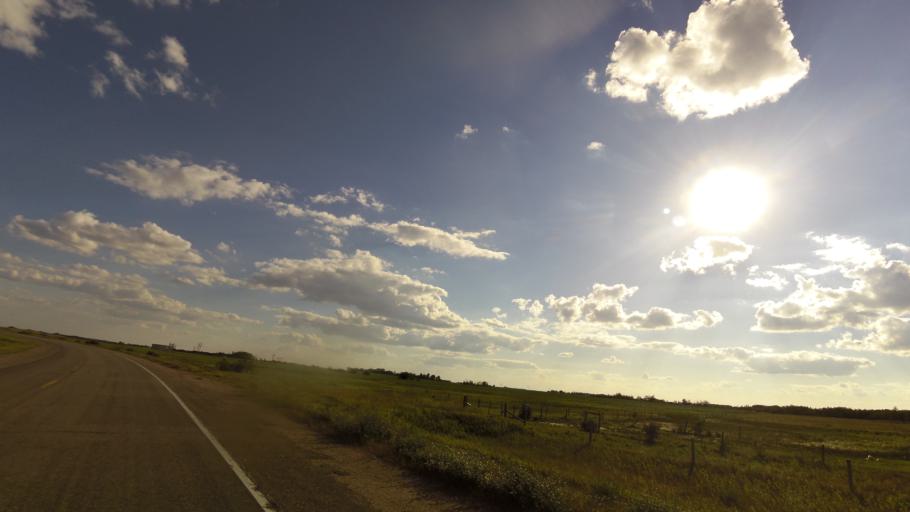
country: CA
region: Saskatchewan
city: Lanigan
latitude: 51.8614
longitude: -105.2158
